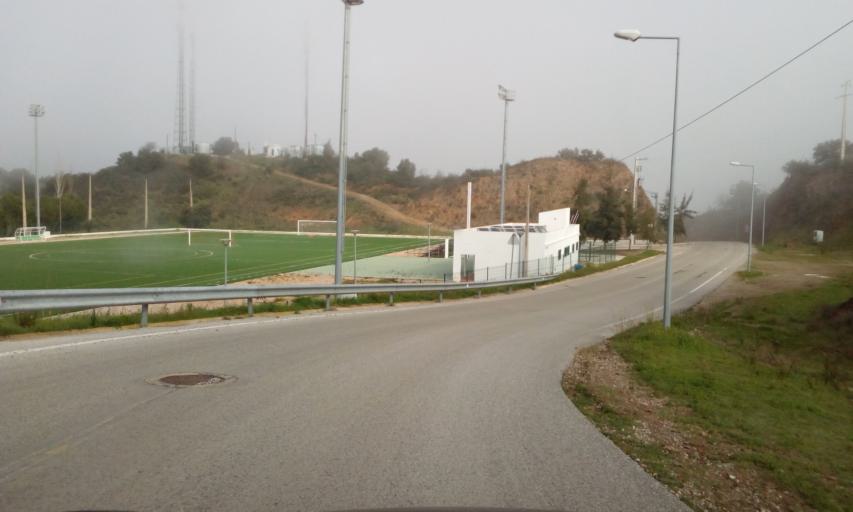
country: PT
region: Faro
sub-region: Alcoutim
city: Alcoutim
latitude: 37.4654
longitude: -7.4749
